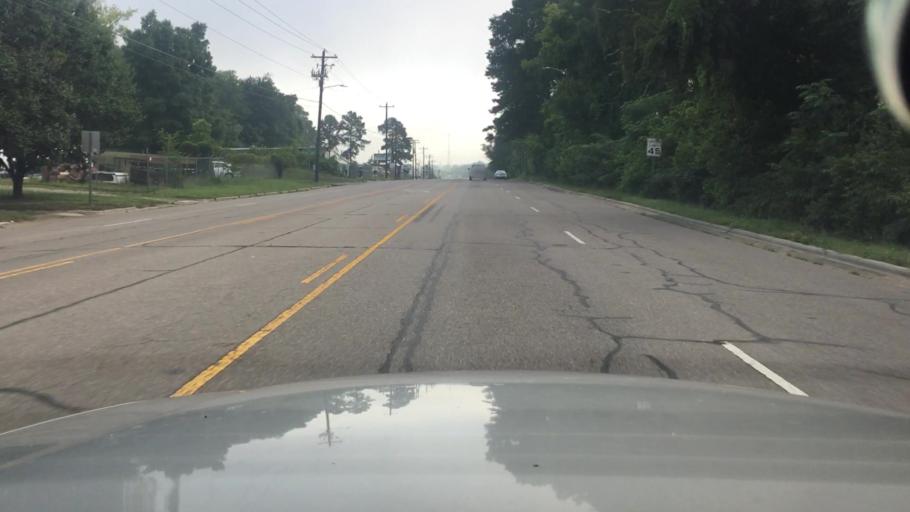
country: US
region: North Carolina
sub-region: Cumberland County
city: Fayetteville
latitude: 35.0297
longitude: -78.8878
